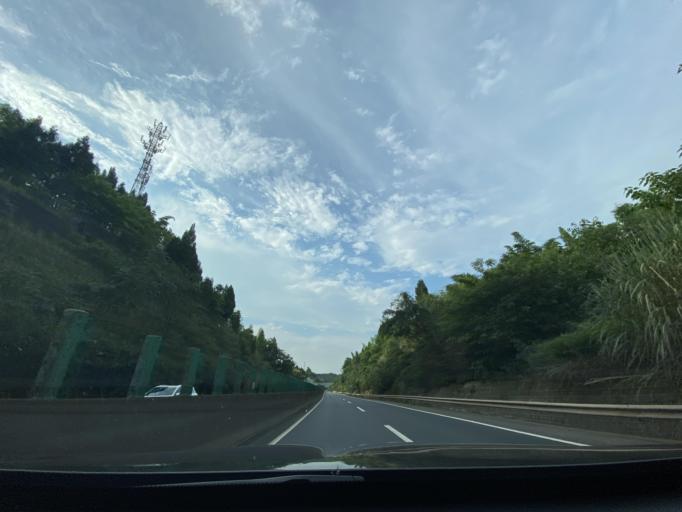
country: CN
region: Sichuan
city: Yanjiang
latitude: 30.0914
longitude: 104.5996
